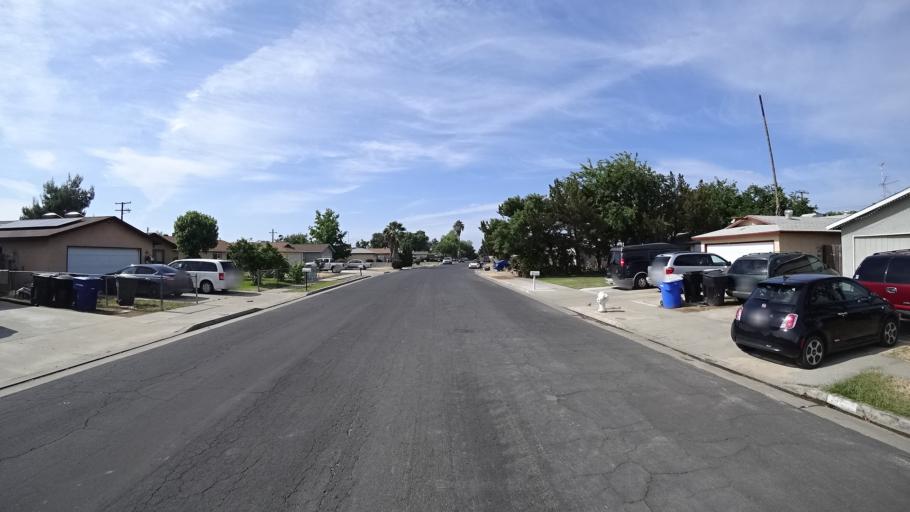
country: US
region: California
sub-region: Kings County
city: Hanford
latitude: 36.3162
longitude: -119.6646
